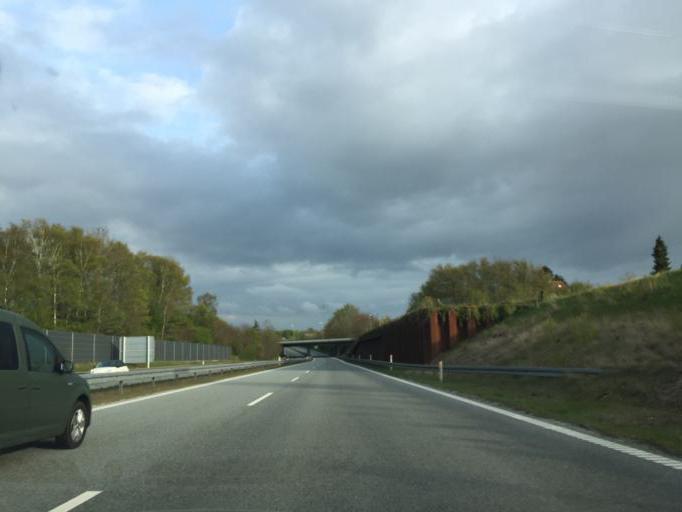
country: DK
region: South Denmark
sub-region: Svendborg Kommune
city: Svendborg
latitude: 55.0683
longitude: 10.5817
